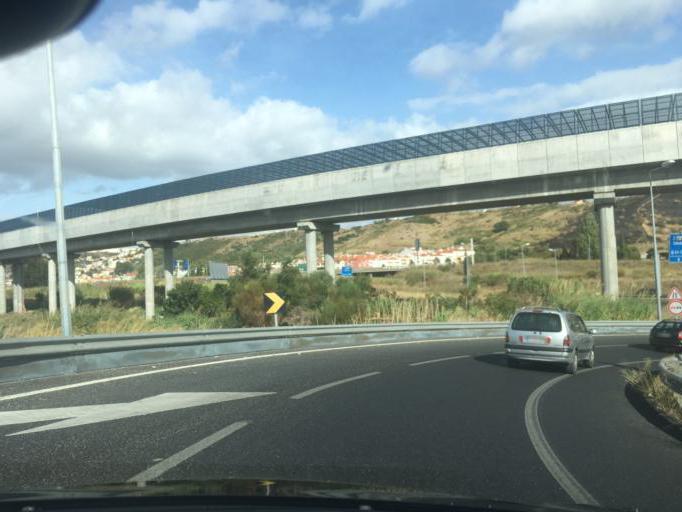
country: PT
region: Lisbon
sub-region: Odivelas
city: Olival do Basto
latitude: 38.7883
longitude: -9.1727
